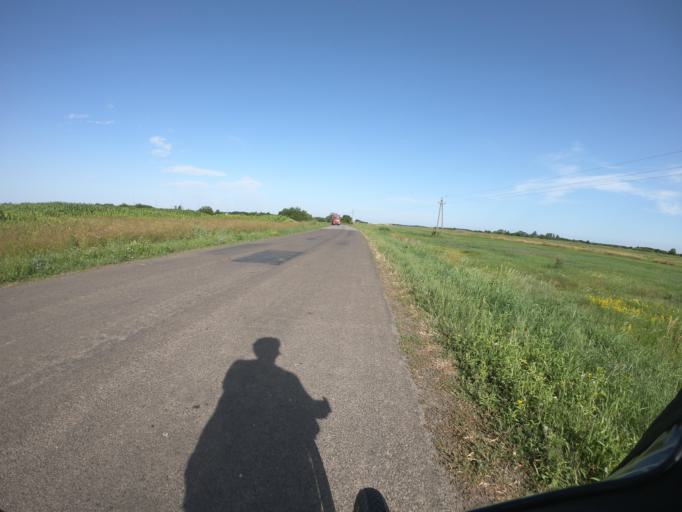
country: HU
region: Hajdu-Bihar
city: Egyek
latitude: 47.6073
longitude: 20.9819
